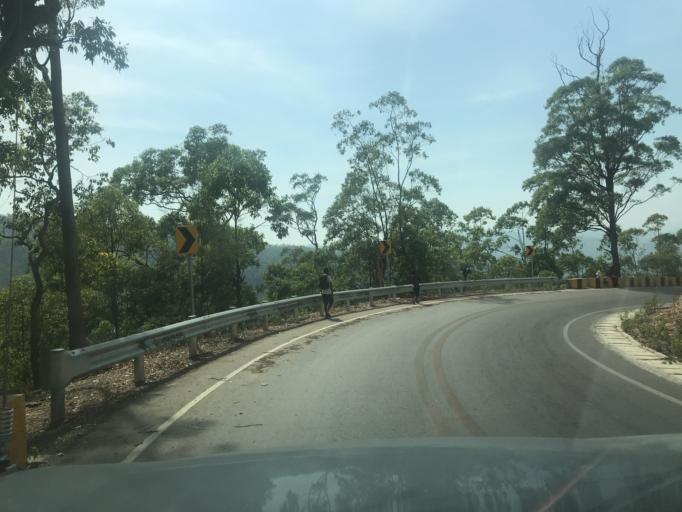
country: TL
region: Aileu
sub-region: Aileu Villa
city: Aileu
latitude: -8.6580
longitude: 125.5609
